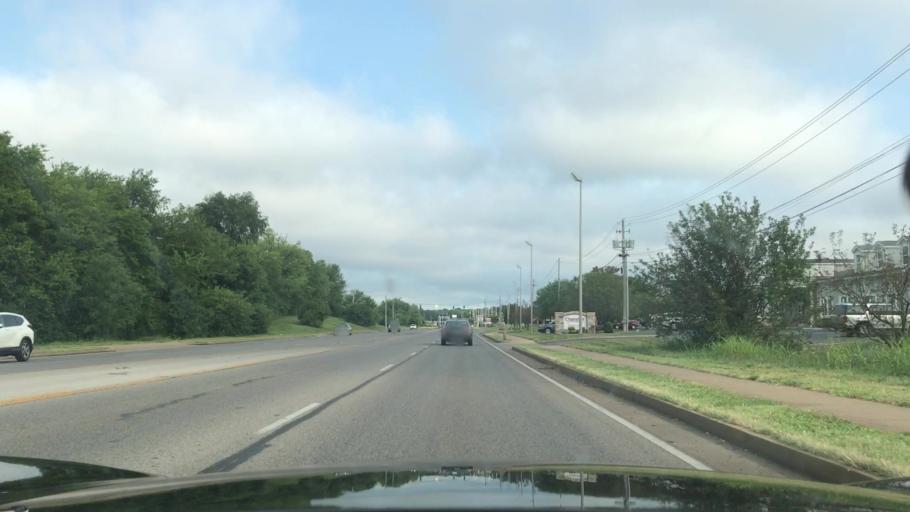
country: US
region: Kentucky
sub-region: Warren County
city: Bowling Green
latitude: 36.9557
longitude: -86.4459
